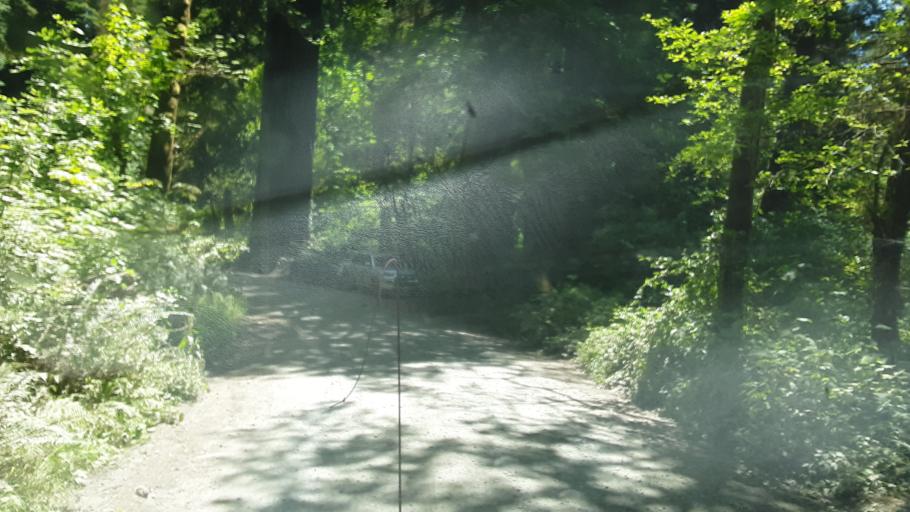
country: US
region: California
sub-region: Del Norte County
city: Bertsch-Oceanview
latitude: 41.8148
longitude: -124.1118
